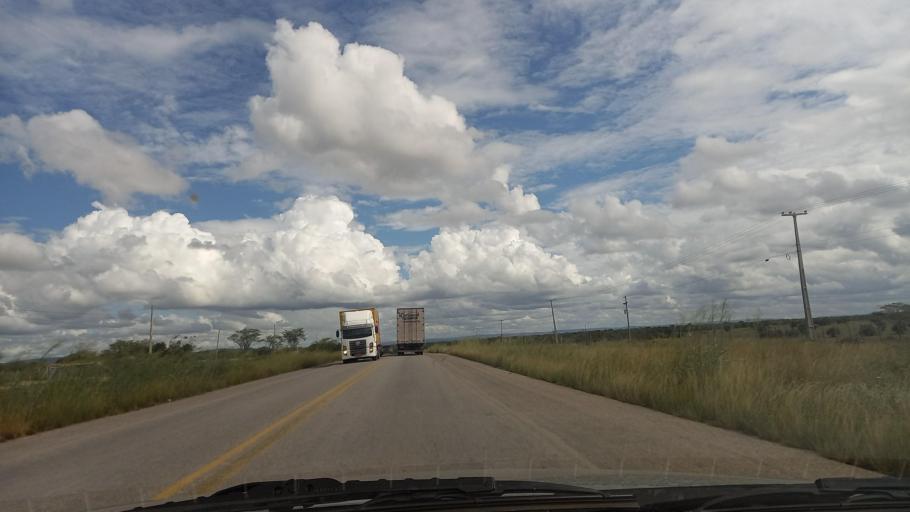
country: BR
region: Pernambuco
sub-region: Cachoeirinha
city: Cachoeirinha
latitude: -8.4184
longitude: -36.1930
